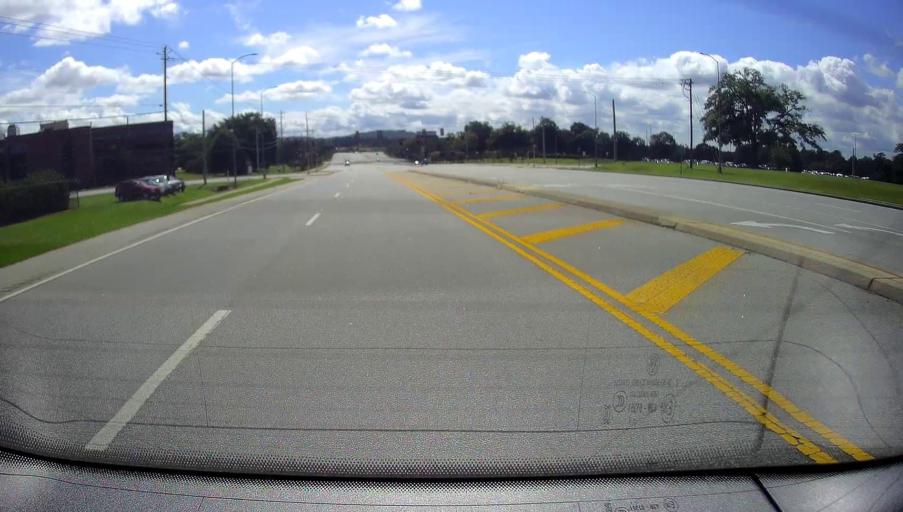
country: US
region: Georgia
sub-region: Bibb County
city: Macon
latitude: 32.8093
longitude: -83.5690
